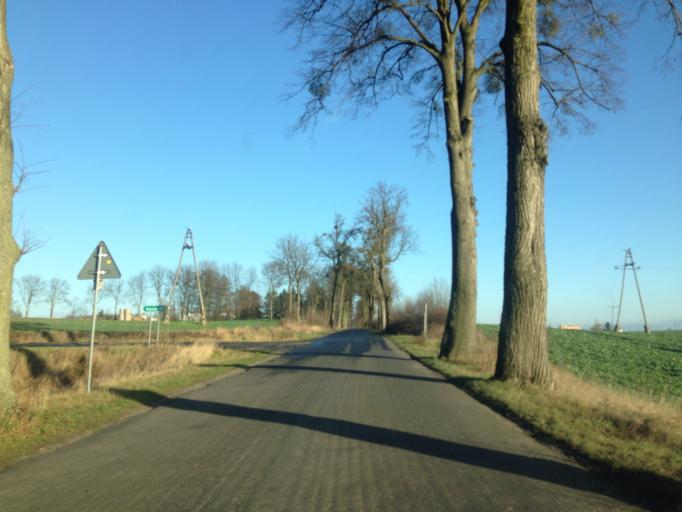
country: PL
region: Kujawsko-Pomorskie
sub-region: Powiat grudziadzki
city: Swiecie nad Osa
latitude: 53.4592
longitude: 19.1539
